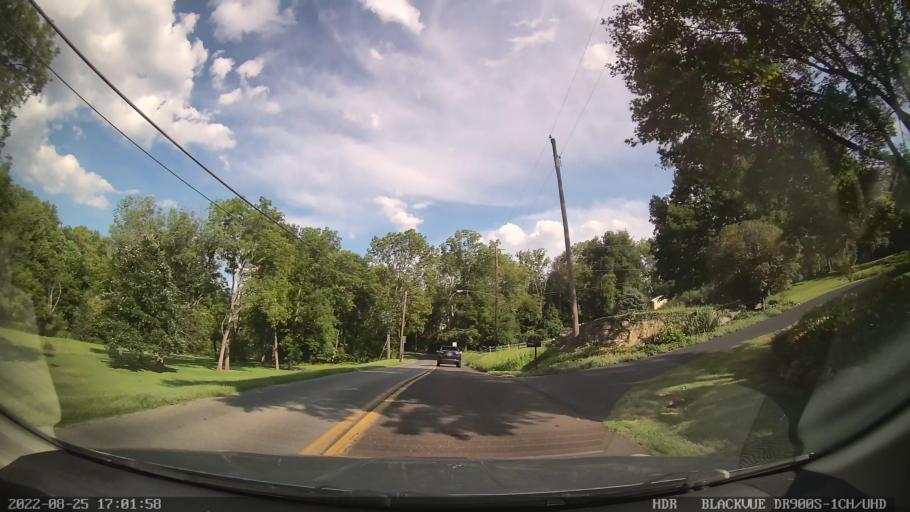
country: US
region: Pennsylvania
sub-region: Lehigh County
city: Emmaus
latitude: 40.5549
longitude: -75.5048
